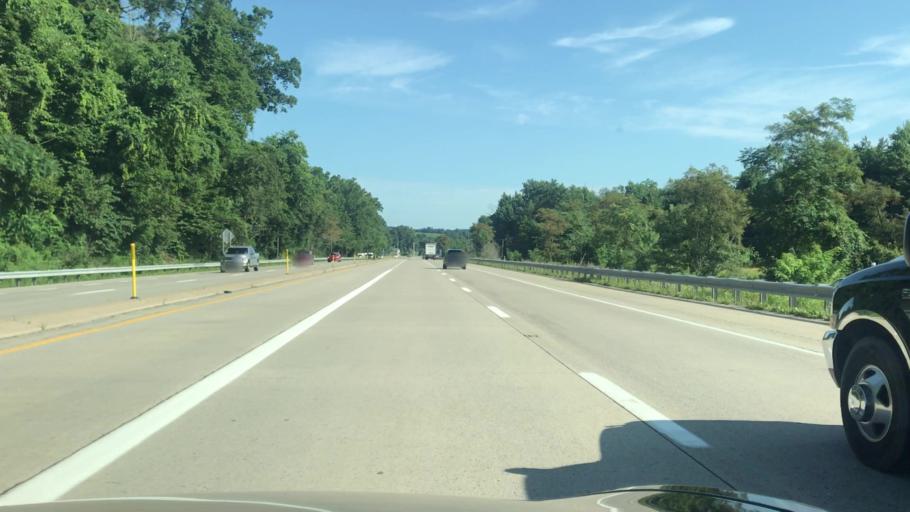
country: US
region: Pennsylvania
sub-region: Dauphin County
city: Millersburg
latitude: 40.5576
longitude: -76.9913
